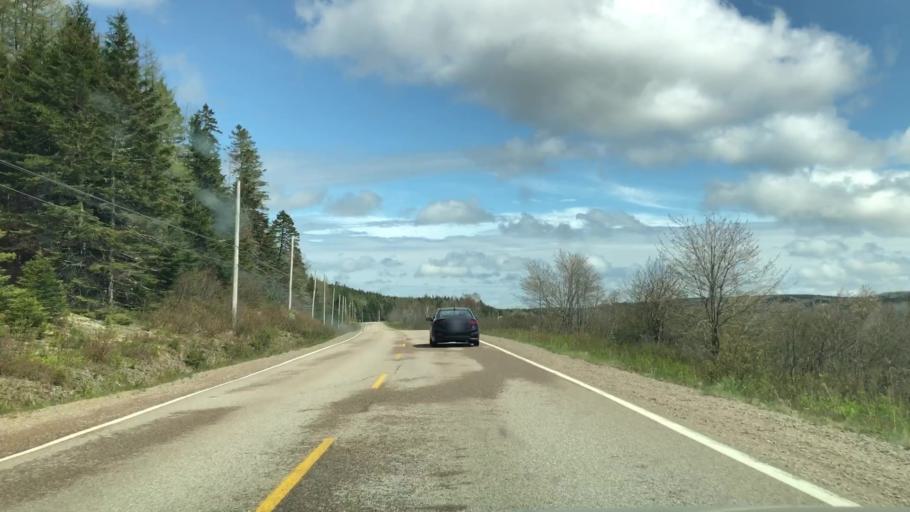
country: CA
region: Nova Scotia
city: Antigonish
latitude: 45.1938
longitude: -61.9969
